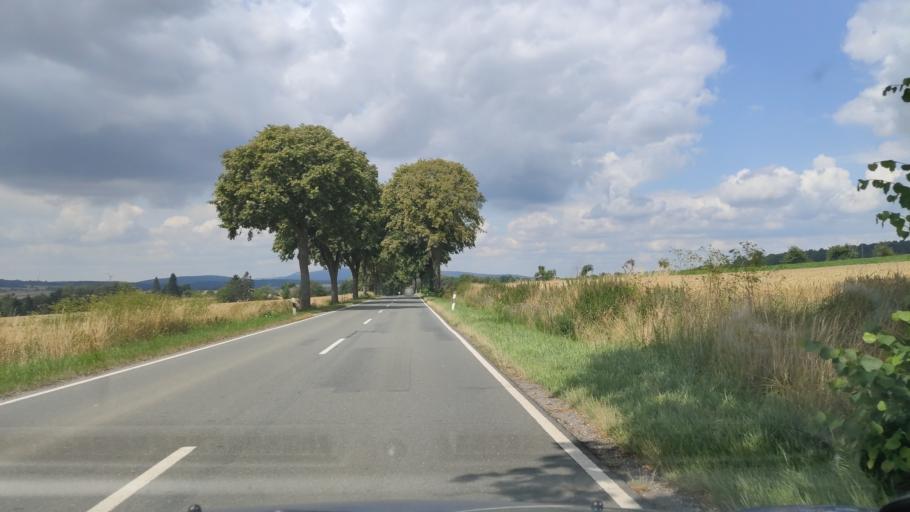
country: DE
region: Lower Saxony
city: Coppenbrugge
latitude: 52.0780
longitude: 9.5093
